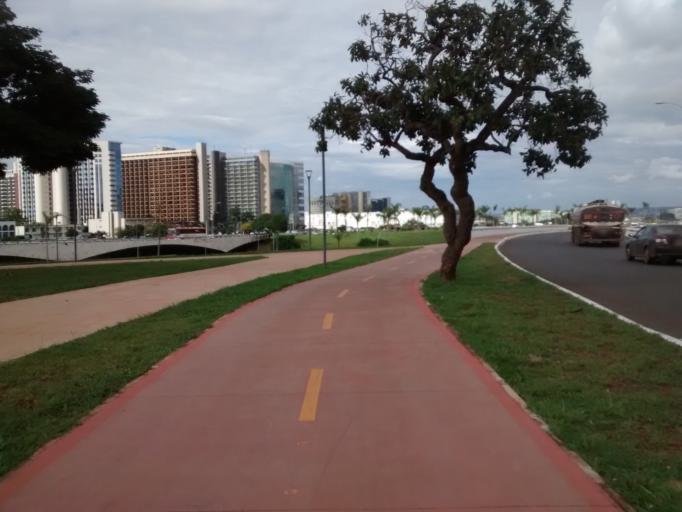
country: BR
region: Federal District
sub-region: Brasilia
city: Brasilia
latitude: -15.7919
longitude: -47.8907
